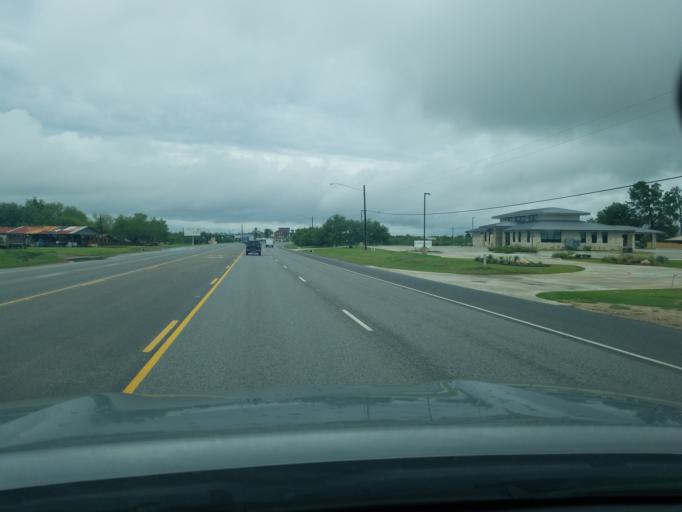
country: US
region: Texas
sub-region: Dimmit County
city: Carrizo Springs
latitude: 28.5370
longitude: -99.8505
